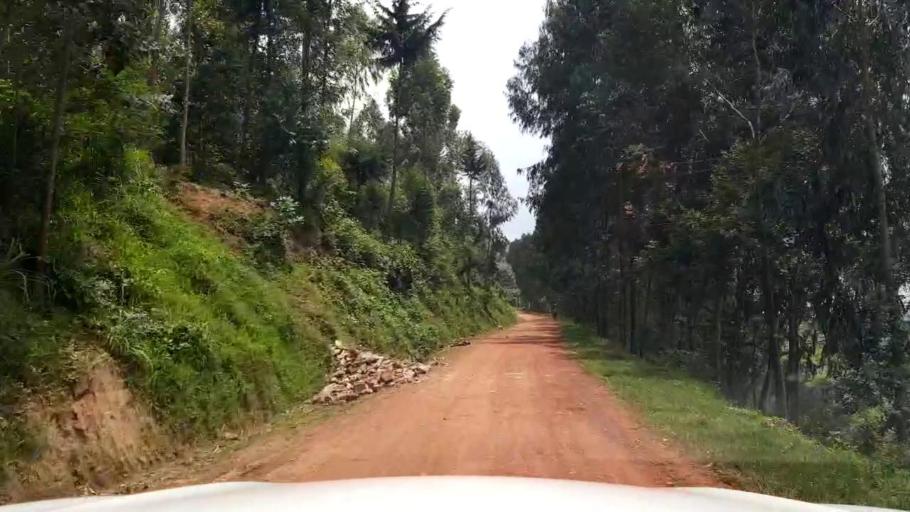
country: RW
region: Northern Province
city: Byumba
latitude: -1.4826
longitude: 29.9227
